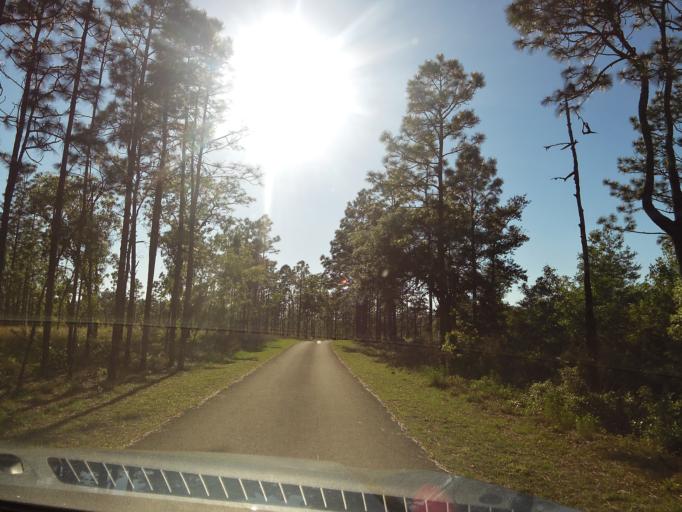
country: US
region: Florida
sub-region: Clay County
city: Keystone Heights
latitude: 29.8333
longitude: -81.9491
